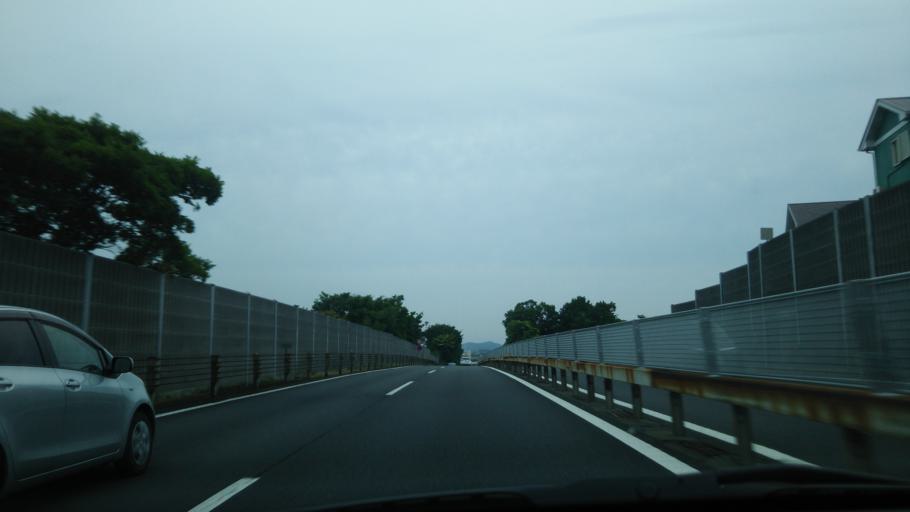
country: JP
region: Kanagawa
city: Oiso
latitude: 35.3421
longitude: 139.2965
